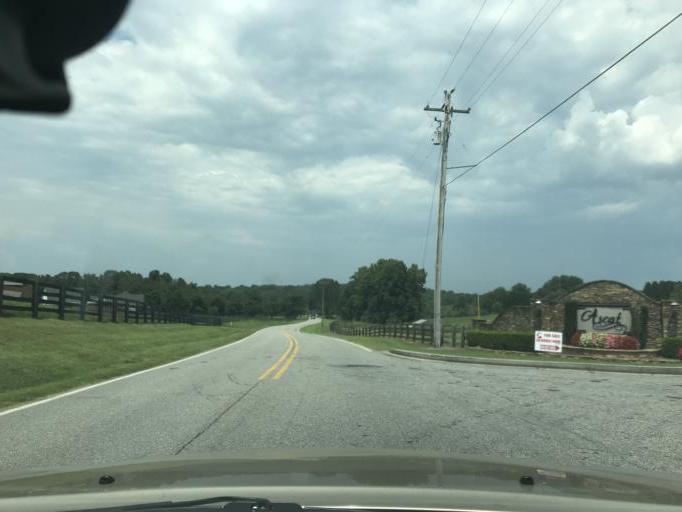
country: US
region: Georgia
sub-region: Forsyth County
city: Cumming
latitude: 34.2814
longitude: -84.2145
